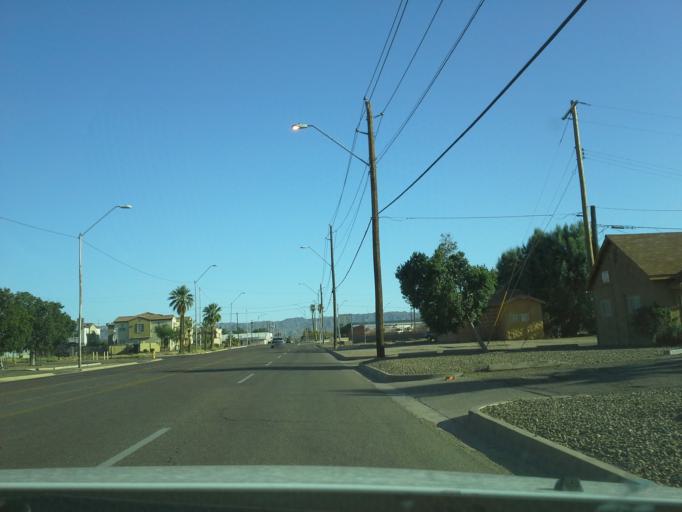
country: US
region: Arizona
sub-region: Maricopa County
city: Phoenix
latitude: 33.4394
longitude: -112.0958
